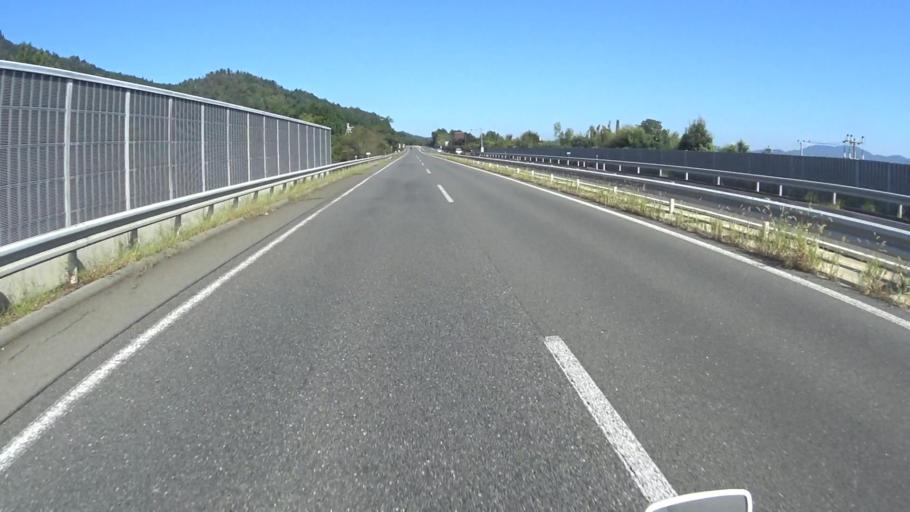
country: JP
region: Kyoto
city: Kameoka
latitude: 35.0349
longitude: 135.5427
